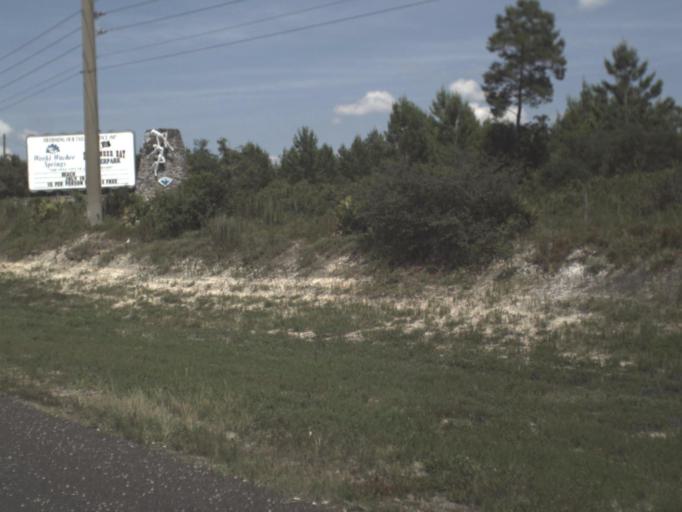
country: US
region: Florida
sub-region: Hernando County
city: North Weeki Wachee
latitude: 28.5122
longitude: -82.5773
